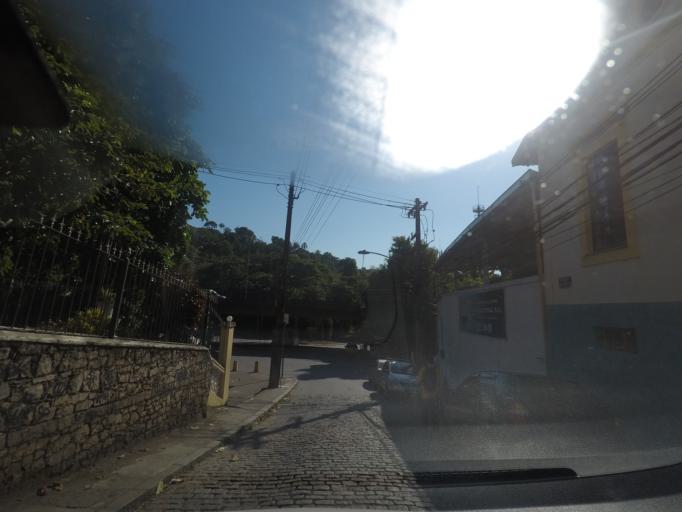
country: BR
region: Rio de Janeiro
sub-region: Rio De Janeiro
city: Rio de Janeiro
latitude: -22.9400
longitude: -43.2031
